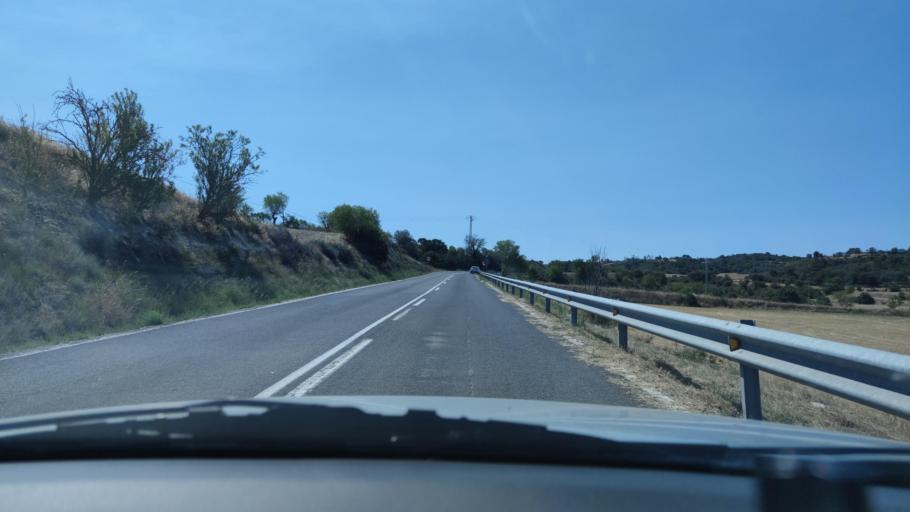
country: ES
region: Catalonia
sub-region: Provincia de Lleida
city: Cervera
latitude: 41.6214
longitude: 1.3380
